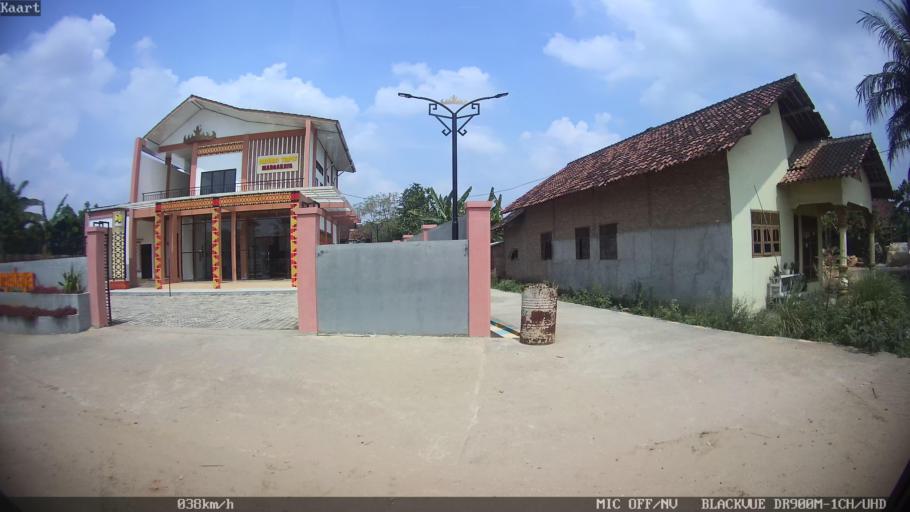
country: ID
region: Lampung
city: Pringsewu
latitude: -5.3847
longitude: 104.9698
